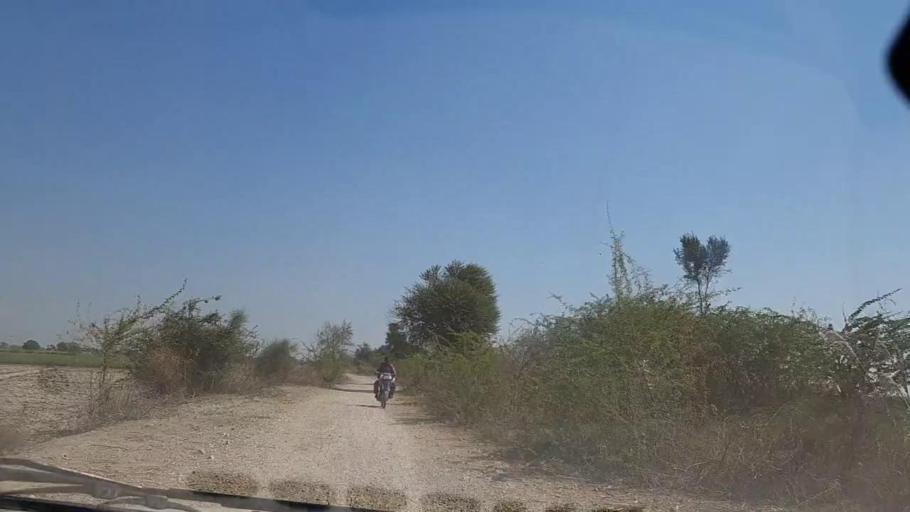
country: PK
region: Sindh
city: Mirpur Khas
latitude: 25.4267
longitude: 69.0318
